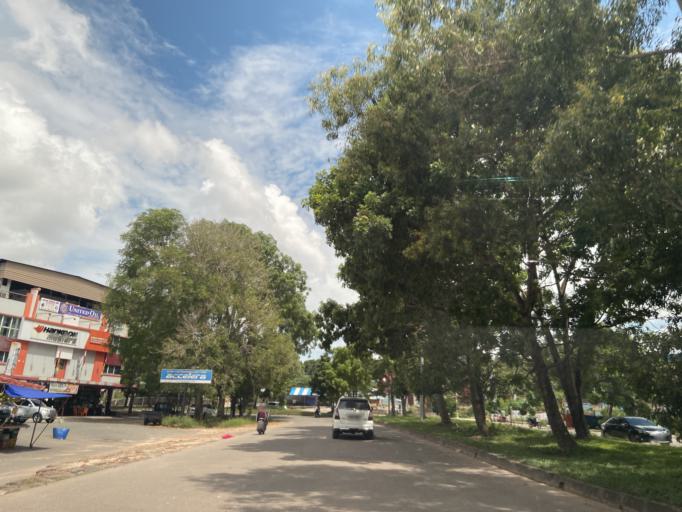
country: SG
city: Singapore
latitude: 1.1402
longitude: 104.0010
